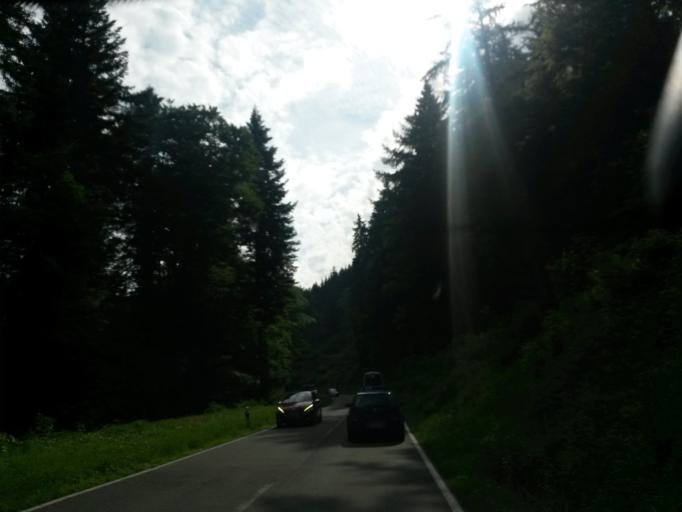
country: DE
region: Baden-Wuerttemberg
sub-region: Karlsruhe Region
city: Oberreichenbach
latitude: 48.7376
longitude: 8.6896
